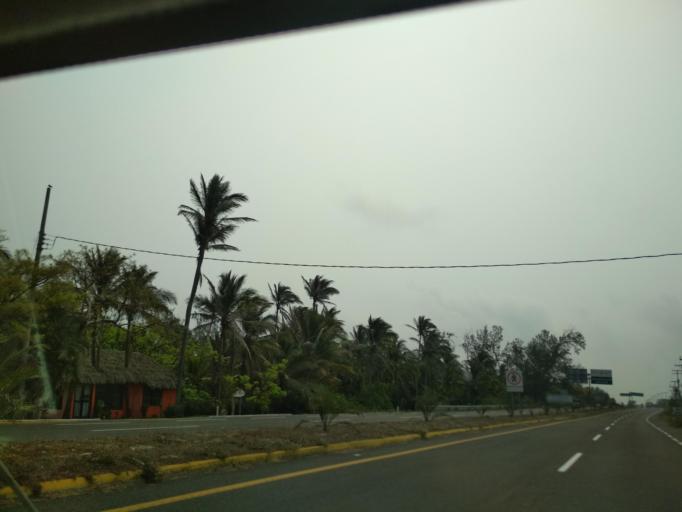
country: MX
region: Veracruz
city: Anton Lizardo
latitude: 19.0522
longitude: -96.0193
